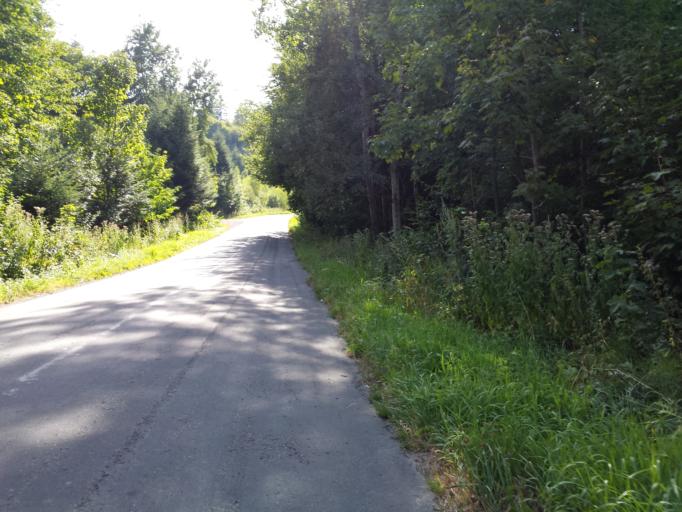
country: PL
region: Subcarpathian Voivodeship
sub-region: Powiat leski
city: Olszanica
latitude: 49.5474
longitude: 22.5315
